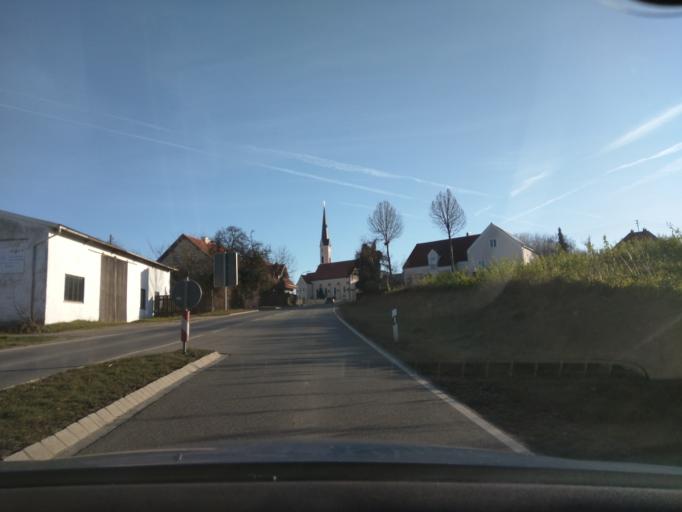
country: DE
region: Bavaria
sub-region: Upper Bavaria
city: Wolfersdorf
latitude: 48.5392
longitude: 11.7522
